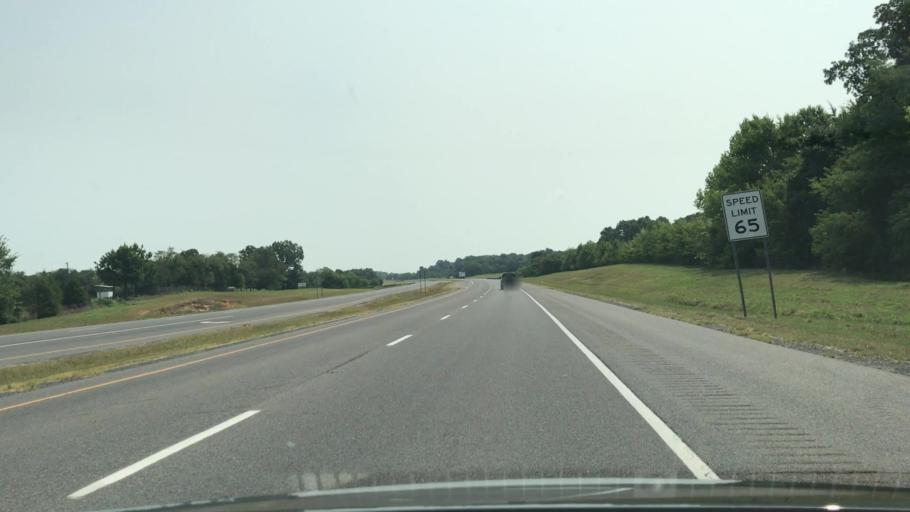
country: US
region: Kentucky
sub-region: Calloway County
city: Murray
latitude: 36.6490
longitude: -88.2491
